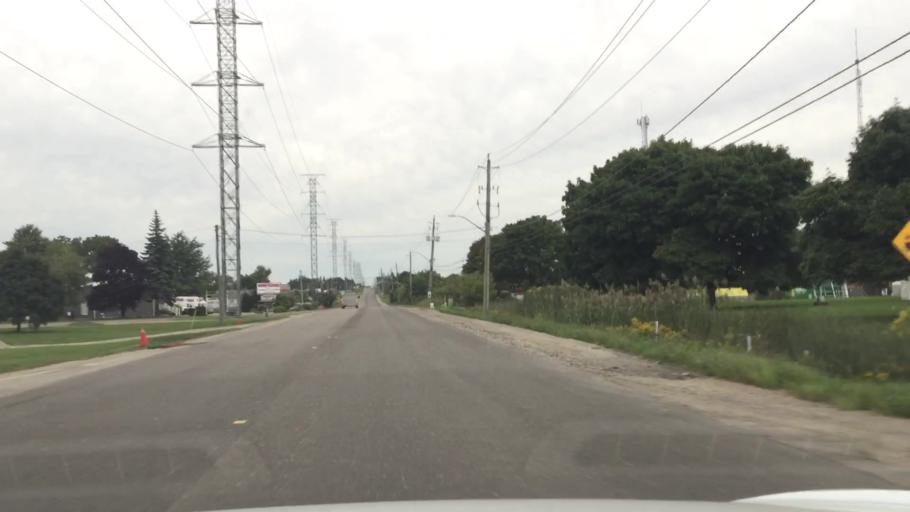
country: CA
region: Ontario
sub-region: Oxford County
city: Woodstock
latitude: 43.1245
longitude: -80.7101
